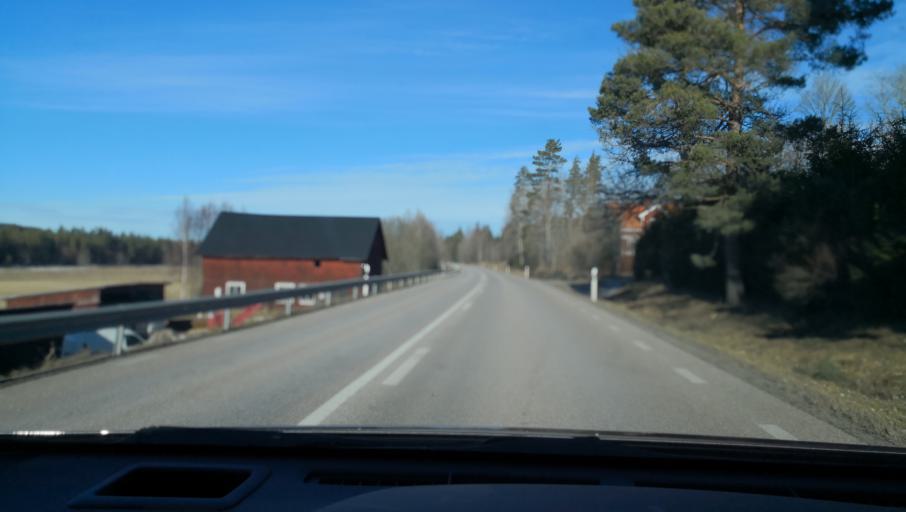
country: SE
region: Uppsala
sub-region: Uppsala Kommun
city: Vattholma
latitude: 60.0766
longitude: 17.7613
